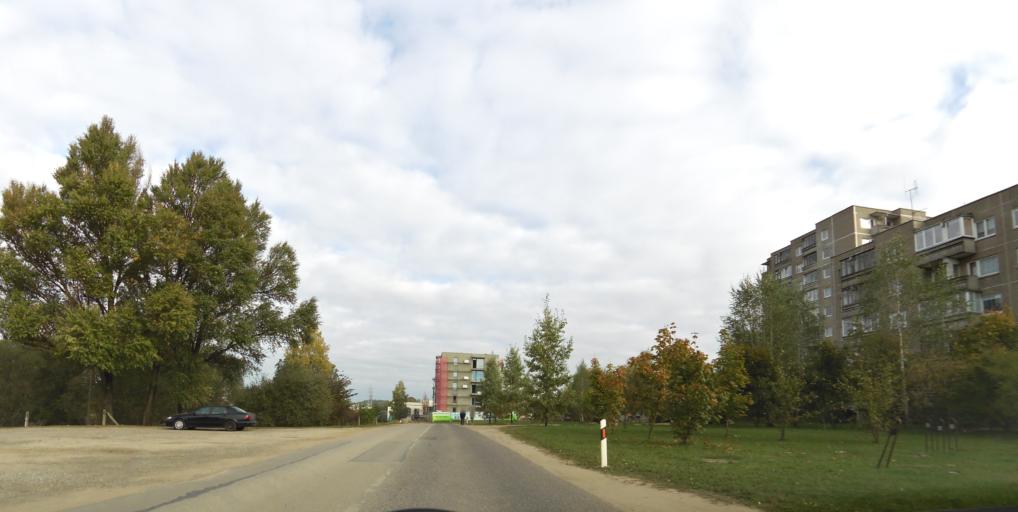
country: LT
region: Vilnius County
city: Justiniskes
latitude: 54.7203
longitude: 25.2108
